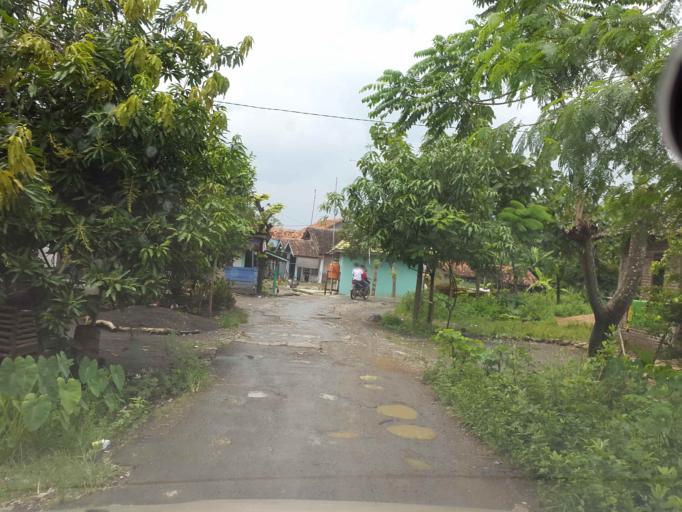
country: ID
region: Central Java
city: Pamedaran
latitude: -7.0568
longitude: 108.9101
